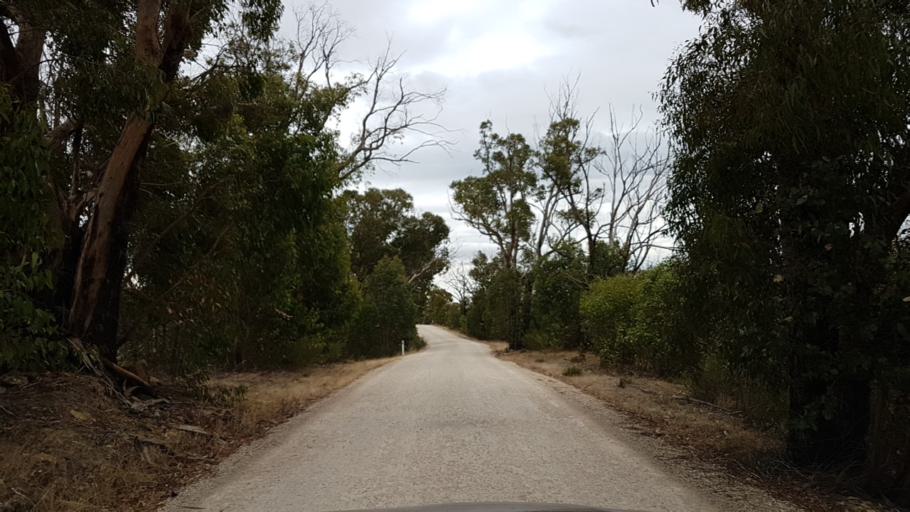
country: AU
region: South Australia
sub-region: Tea Tree Gully
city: Golden Grove
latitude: -34.7770
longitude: 138.8128
